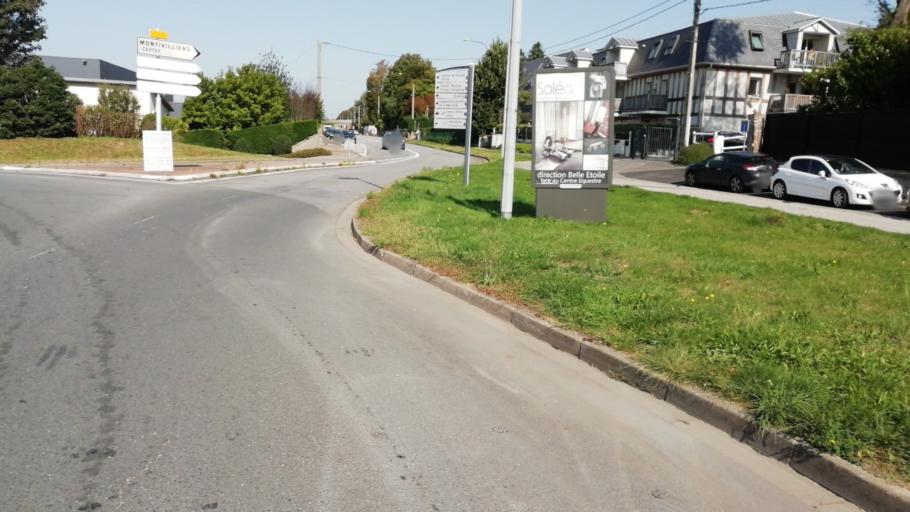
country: FR
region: Haute-Normandie
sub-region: Departement de la Seine-Maritime
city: Montivilliers
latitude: 49.5305
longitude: 0.1900
